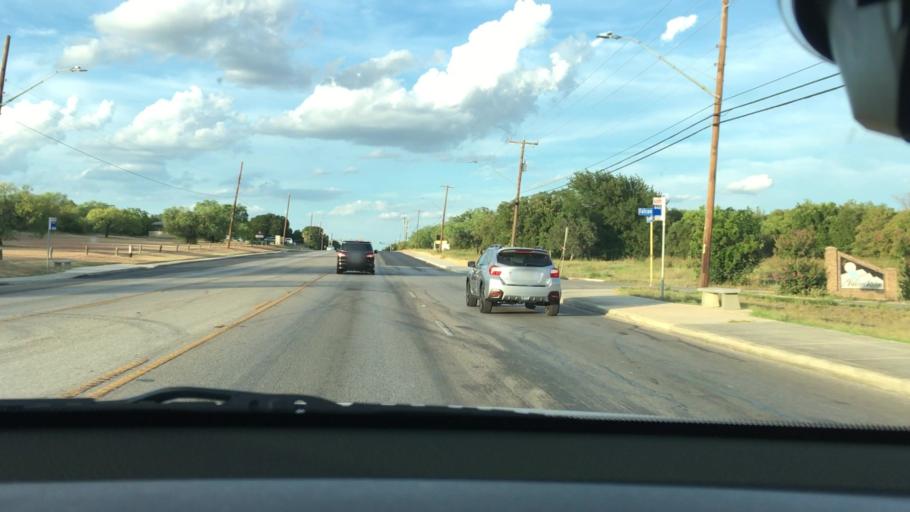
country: US
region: Texas
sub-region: Bexar County
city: Live Oak
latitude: 29.5826
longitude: -98.3681
